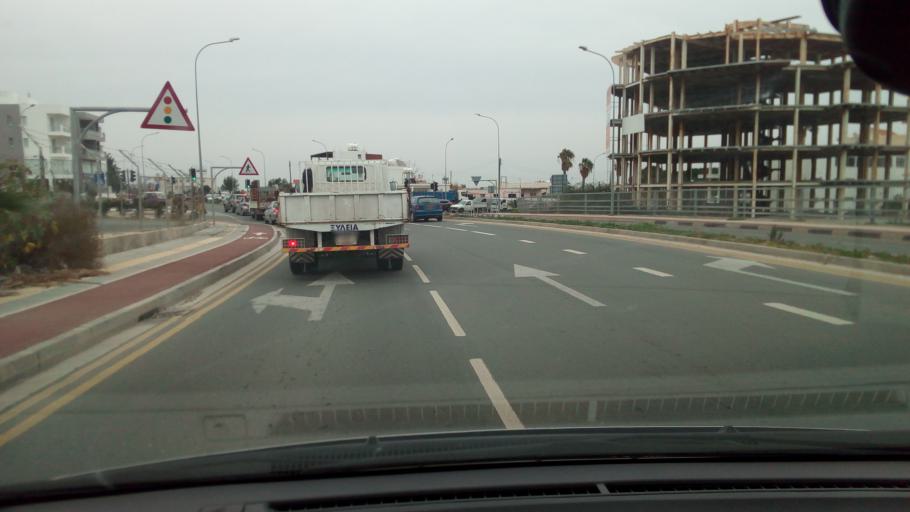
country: CY
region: Pafos
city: Empa
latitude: 34.7929
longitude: 32.4352
